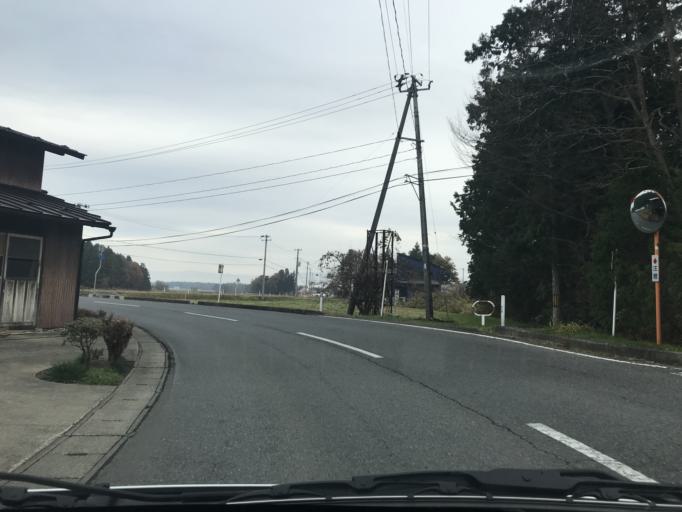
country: JP
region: Iwate
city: Mizusawa
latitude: 39.1058
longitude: 141.1064
